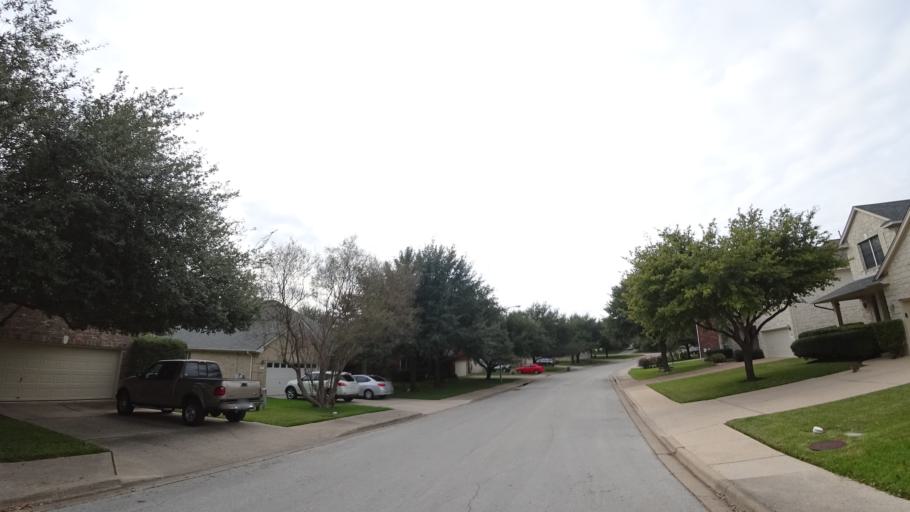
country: US
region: Texas
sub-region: Travis County
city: Wells Branch
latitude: 30.4491
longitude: -97.6824
